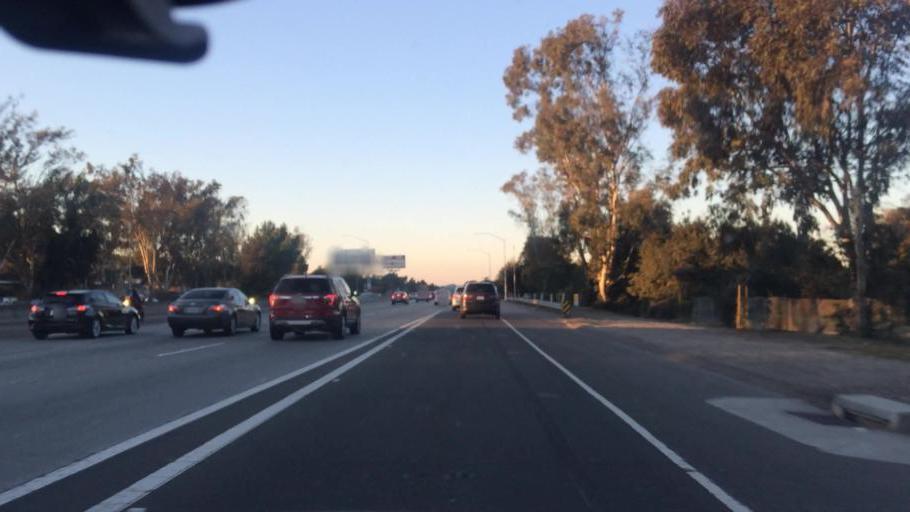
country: US
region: California
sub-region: Contra Costa County
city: San Ramon
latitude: 37.7814
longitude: -121.9771
